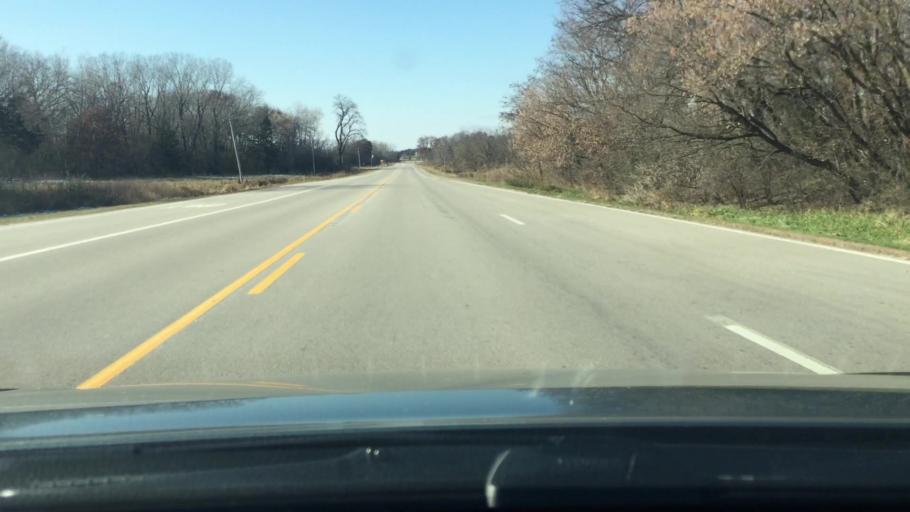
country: US
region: Wisconsin
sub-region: Jefferson County
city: Lake Ripley
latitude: 43.0077
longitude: -88.9364
